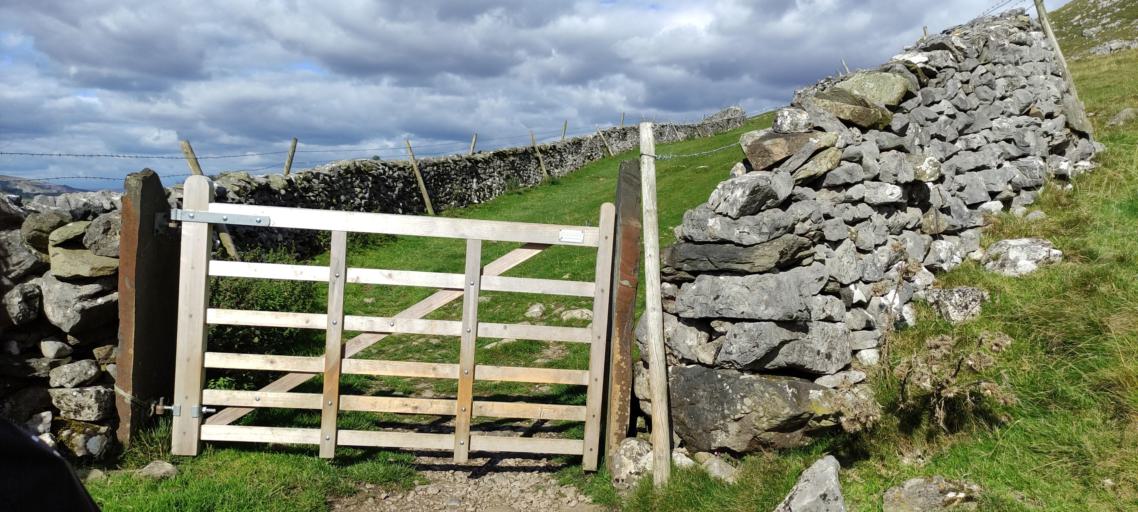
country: GB
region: England
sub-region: North Yorkshire
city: Settle
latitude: 54.0739
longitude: -2.2716
